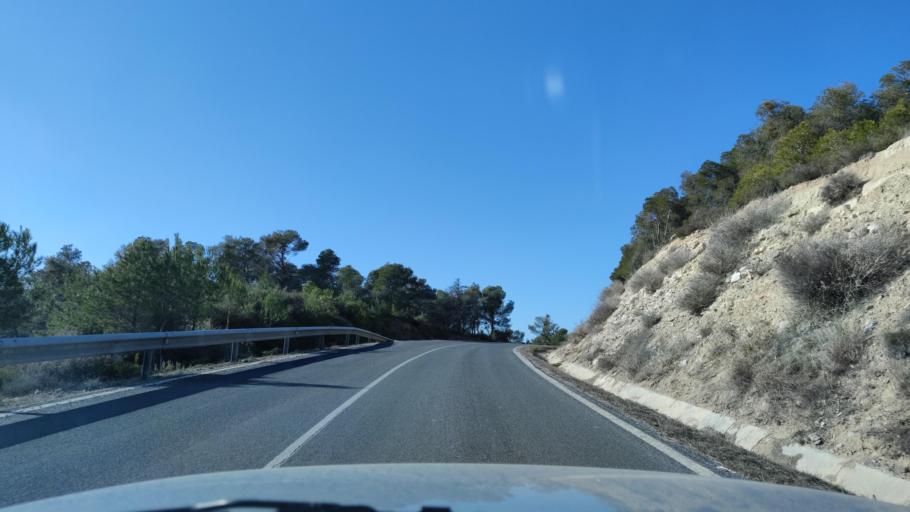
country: ES
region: Catalonia
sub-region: Provincia de Lleida
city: Maials
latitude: 41.3293
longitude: 0.4361
